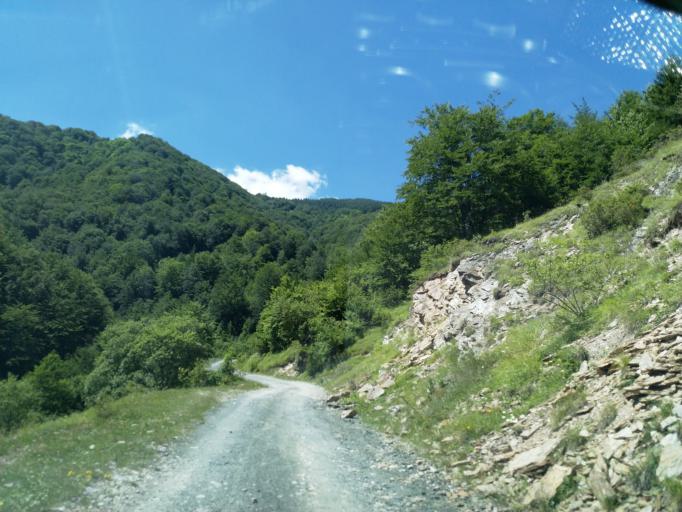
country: XK
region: Mitrovica
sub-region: Komuna e Leposaviqit
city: Leposaviq
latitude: 43.2672
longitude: 20.8593
